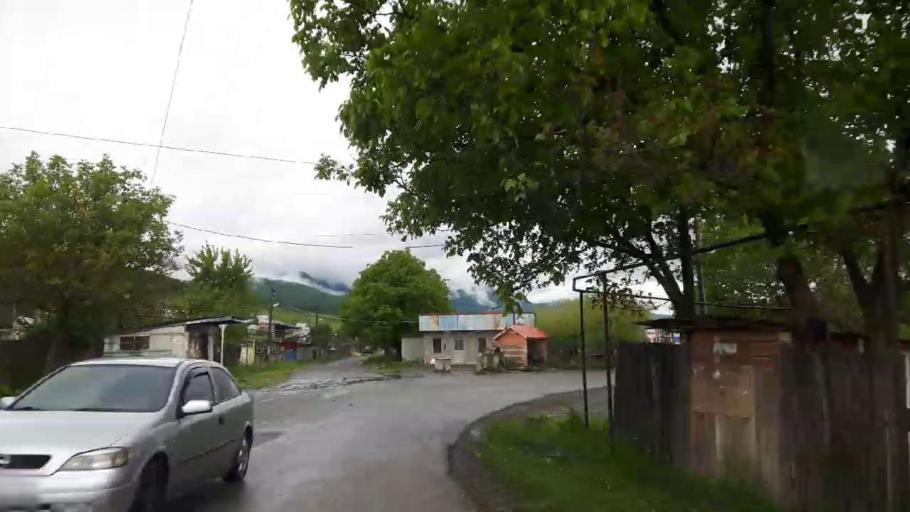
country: GE
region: Shida Kartli
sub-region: Khashuris Raioni
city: Khashuri
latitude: 41.9842
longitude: 43.6637
